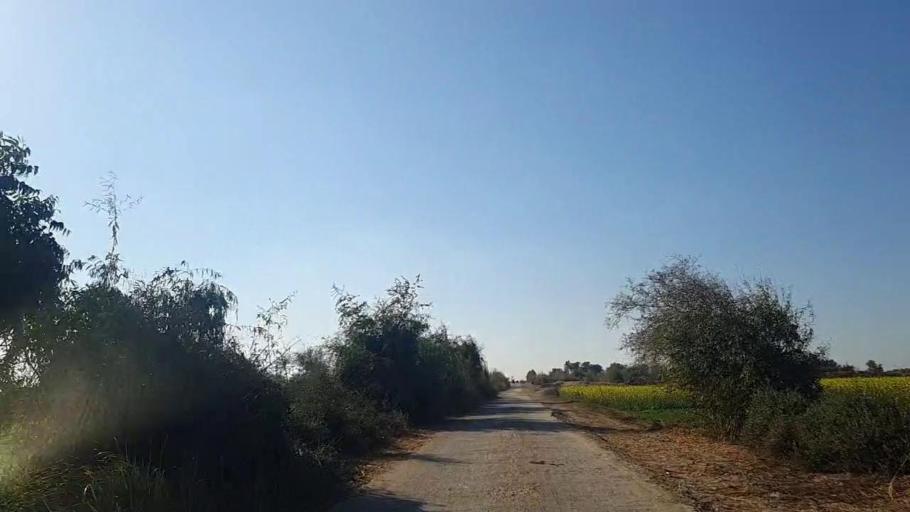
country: PK
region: Sindh
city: Sanghar
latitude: 26.2413
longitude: 68.9016
